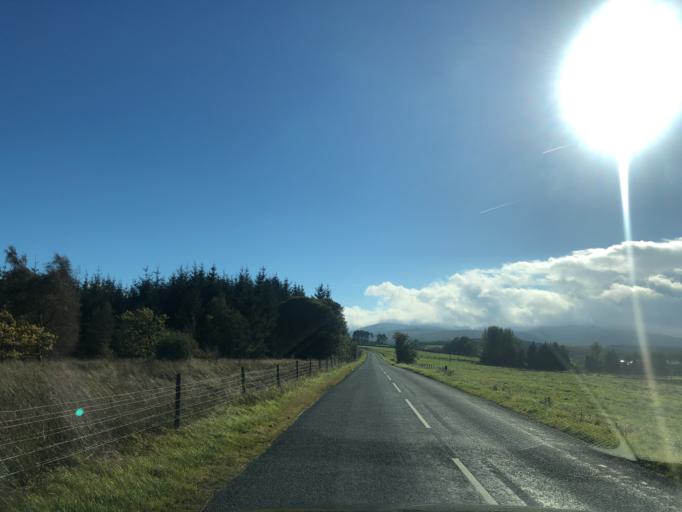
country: GB
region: England
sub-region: Cumbria
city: Keswick
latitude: 54.6257
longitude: -2.9497
